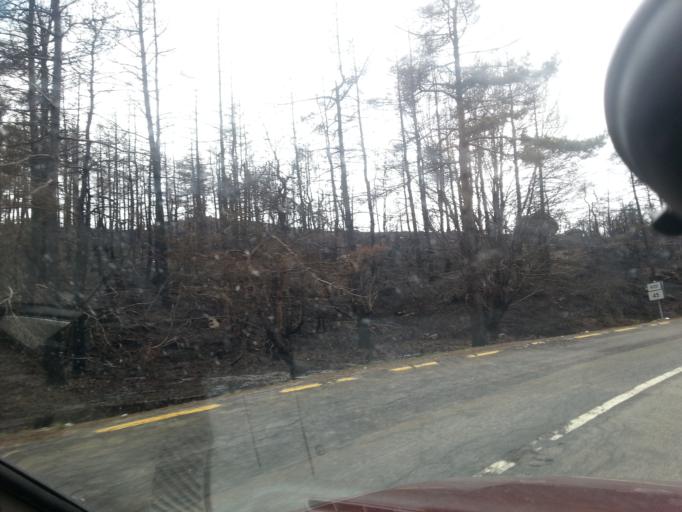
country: PT
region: Guarda
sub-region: Manteigas
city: Manteigas
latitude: 40.4124
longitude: -7.5778
